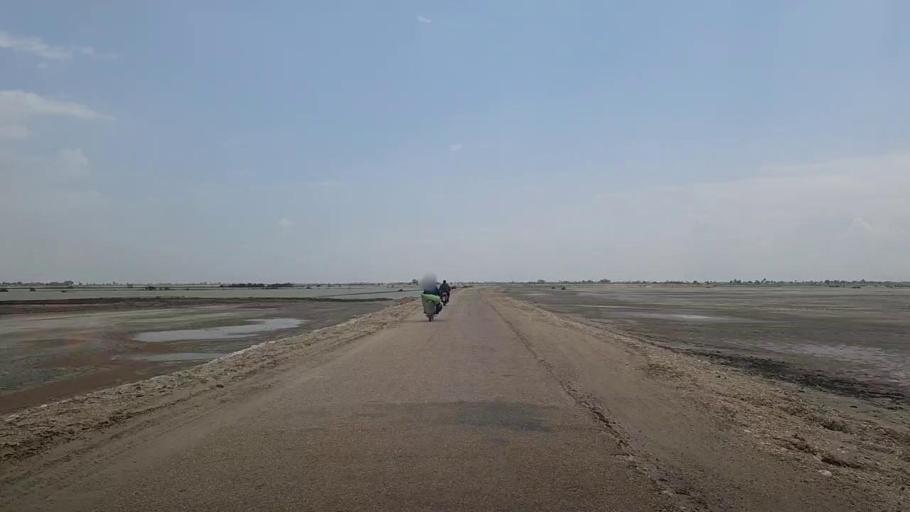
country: PK
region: Sindh
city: Kandhkot
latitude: 28.2870
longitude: 69.1526
